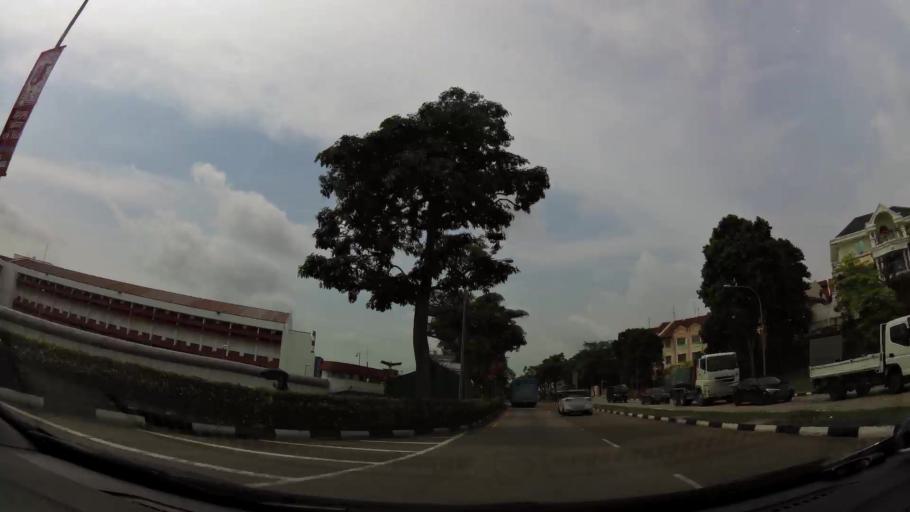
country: SG
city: Singapore
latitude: 1.3616
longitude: 103.9717
